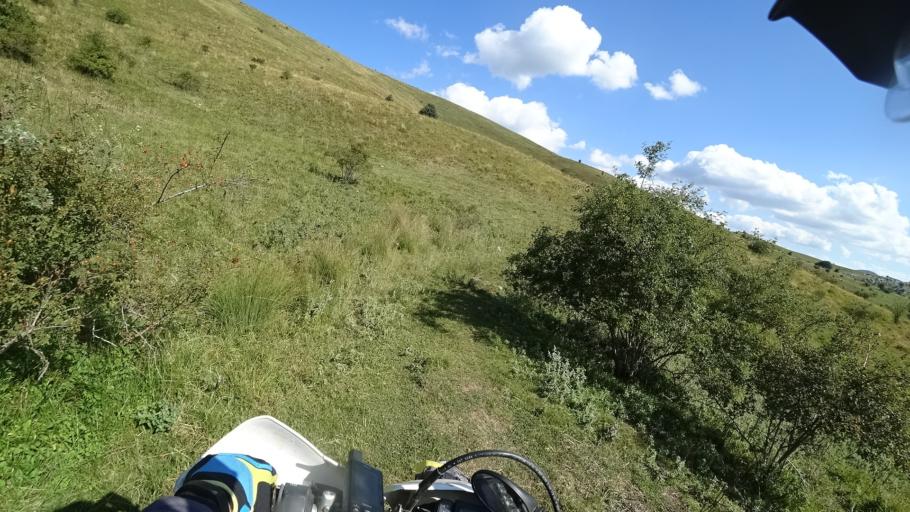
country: HR
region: Zadarska
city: Gracac
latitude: 44.4019
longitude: 16.0087
